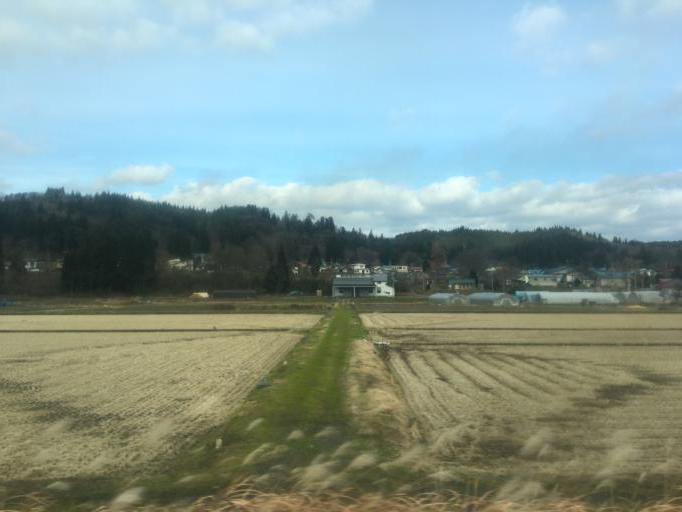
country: JP
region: Akita
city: Takanosu
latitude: 40.2251
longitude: 140.3356
